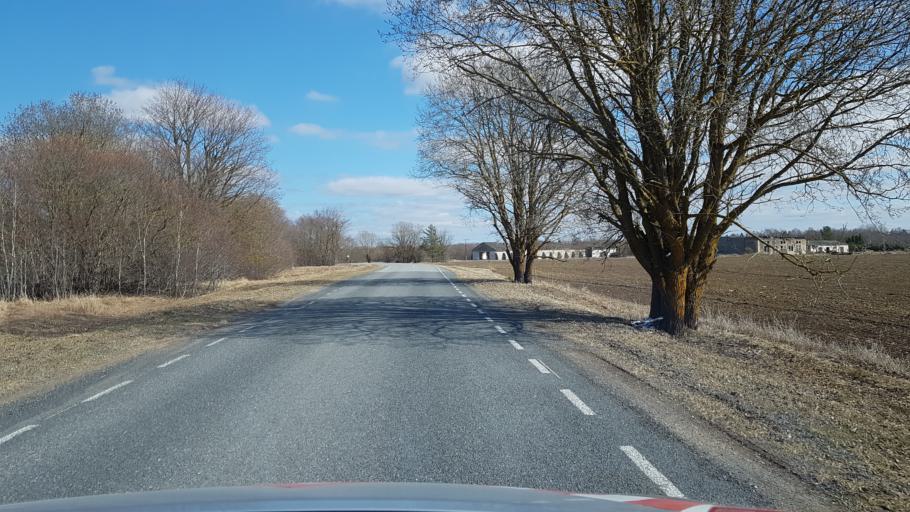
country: EE
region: Laeaene-Virumaa
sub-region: Tapa vald
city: Tapa
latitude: 59.2542
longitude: 25.8360
